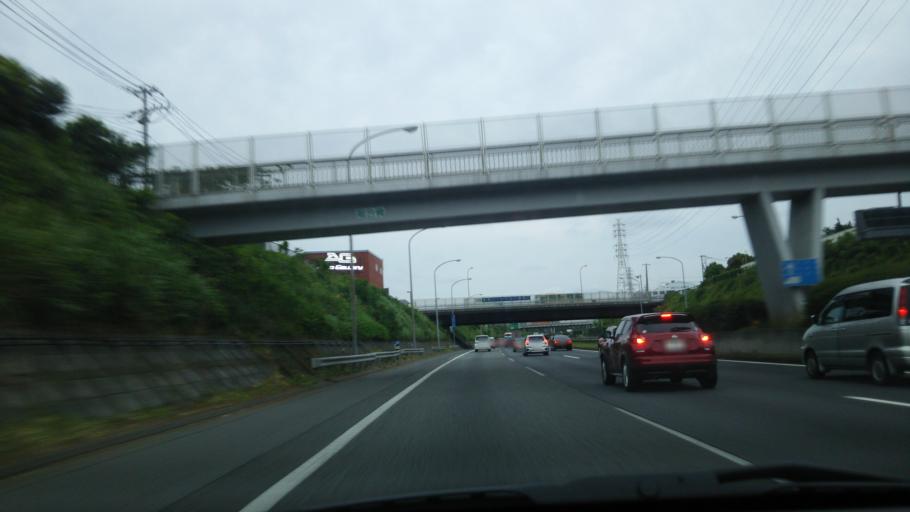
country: JP
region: Kanagawa
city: Minami-rinkan
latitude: 35.4967
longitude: 139.4739
